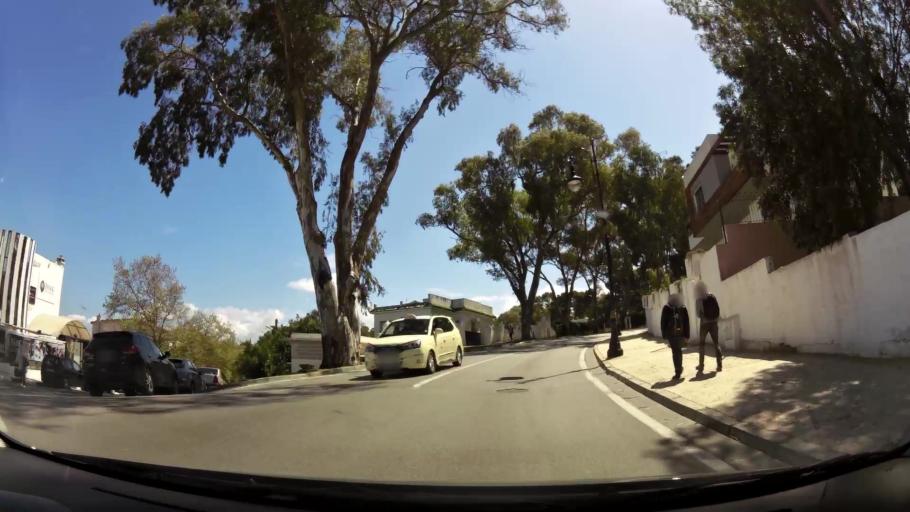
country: MA
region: Tanger-Tetouan
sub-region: Tanger-Assilah
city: Tangier
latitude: 35.7803
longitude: -5.8344
